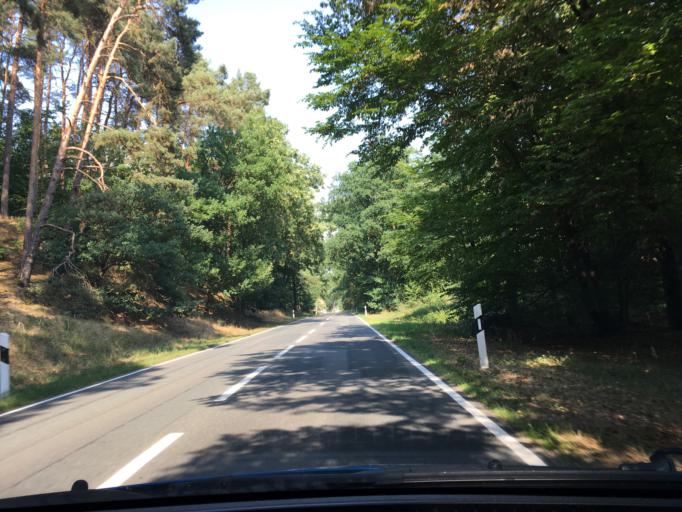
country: DE
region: Lower Saxony
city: Tosterglope
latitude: 53.2369
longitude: 10.8386
